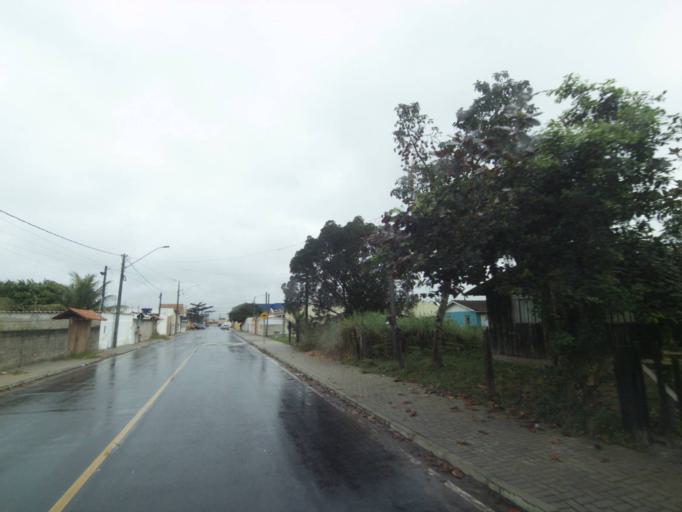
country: BR
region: Parana
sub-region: Paranagua
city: Paranagua
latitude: -25.5714
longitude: -48.5728
